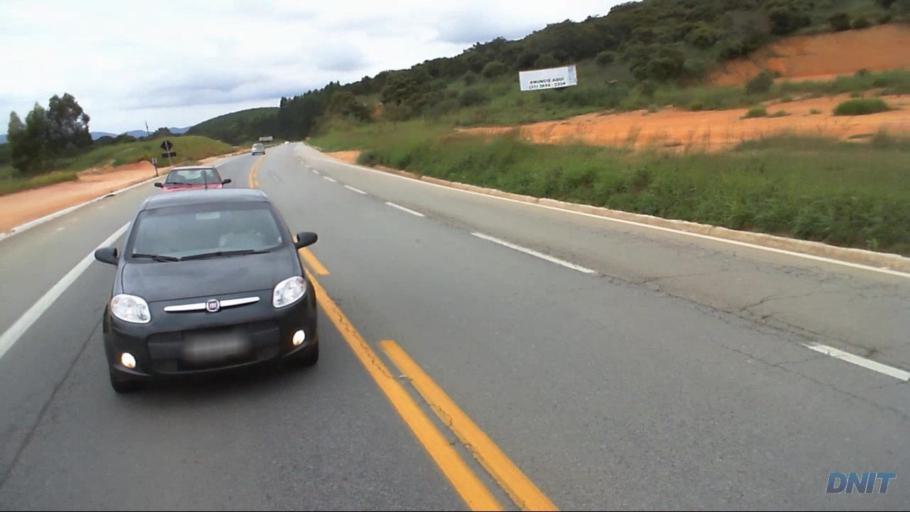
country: BR
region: Minas Gerais
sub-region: Barao De Cocais
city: Barao de Cocais
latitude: -19.7619
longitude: -43.4602
